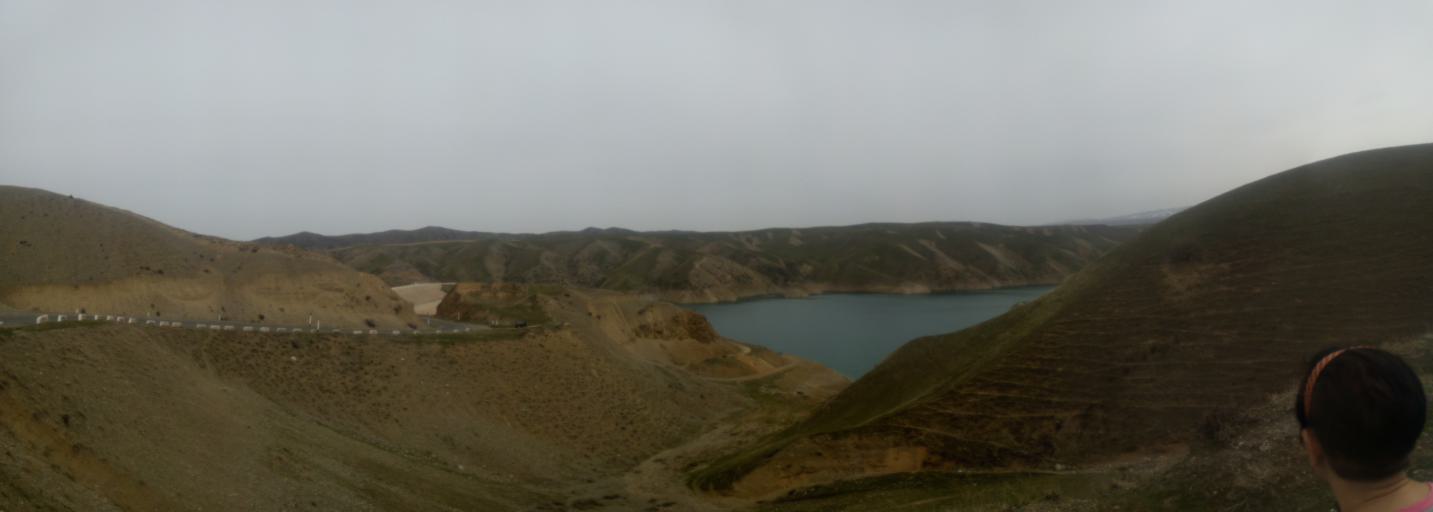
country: UZ
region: Jizzax
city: Zomin
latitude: 39.8488
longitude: 68.3745
